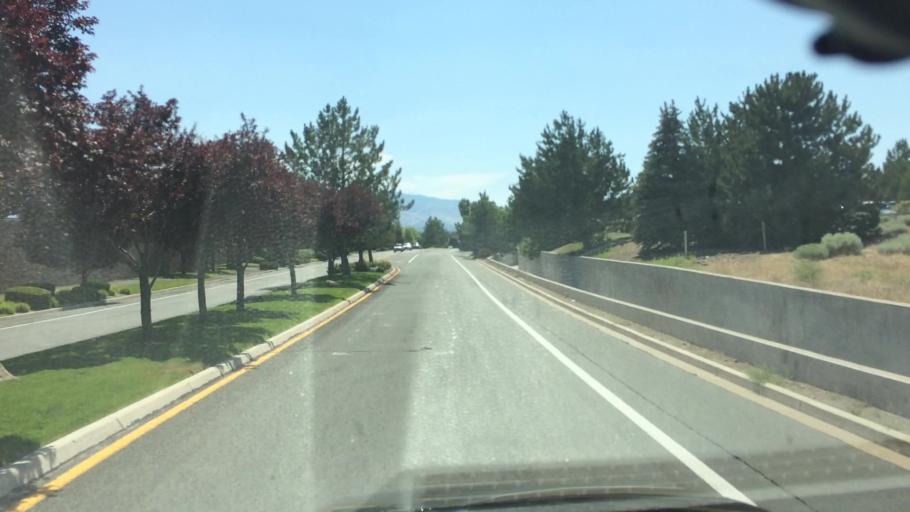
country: US
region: Nevada
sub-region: Washoe County
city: Sparks
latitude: 39.5657
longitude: -119.7019
